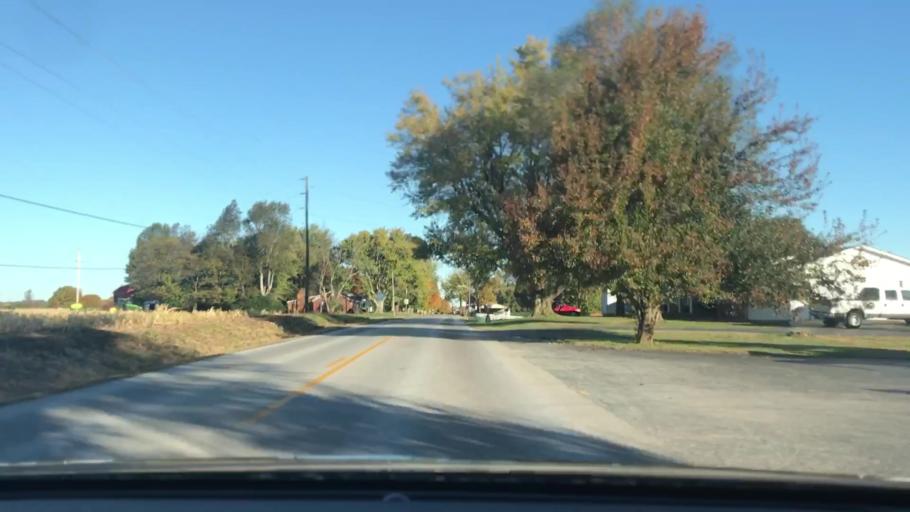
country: US
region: Kentucky
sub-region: Logan County
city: Auburn
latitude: 36.8540
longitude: -86.7078
